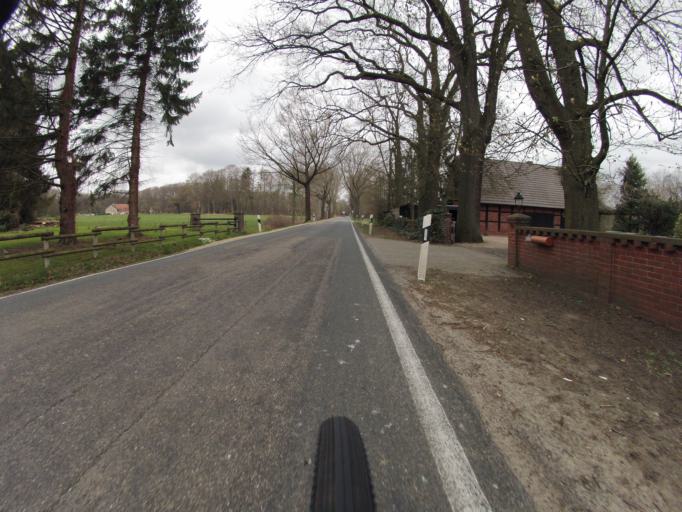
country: DE
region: North Rhine-Westphalia
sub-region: Regierungsbezirk Munster
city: Mettingen
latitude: 52.3029
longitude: 7.8178
